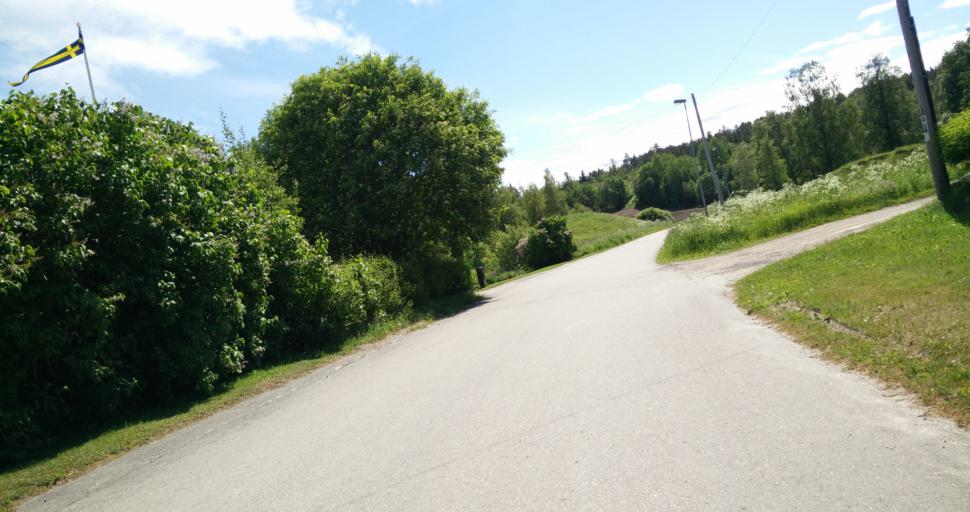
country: SE
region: Vaesternorrland
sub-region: Sundsvalls Kommun
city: Nolby
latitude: 62.2868
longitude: 17.3675
